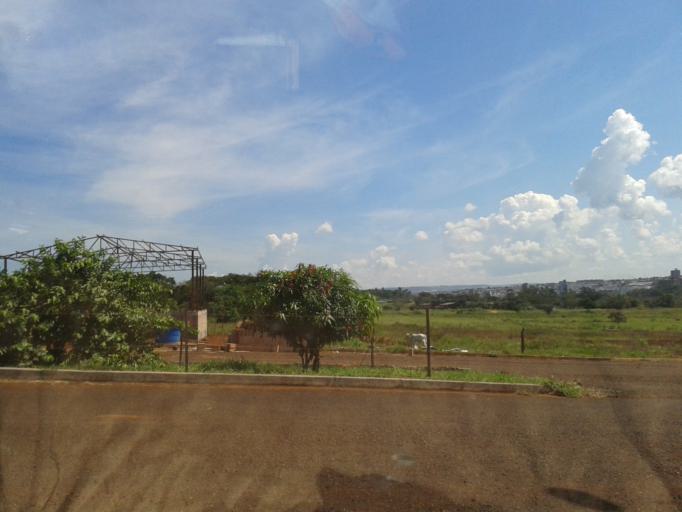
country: BR
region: Goias
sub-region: Itumbiara
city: Itumbiara
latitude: -18.4245
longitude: -49.1859
